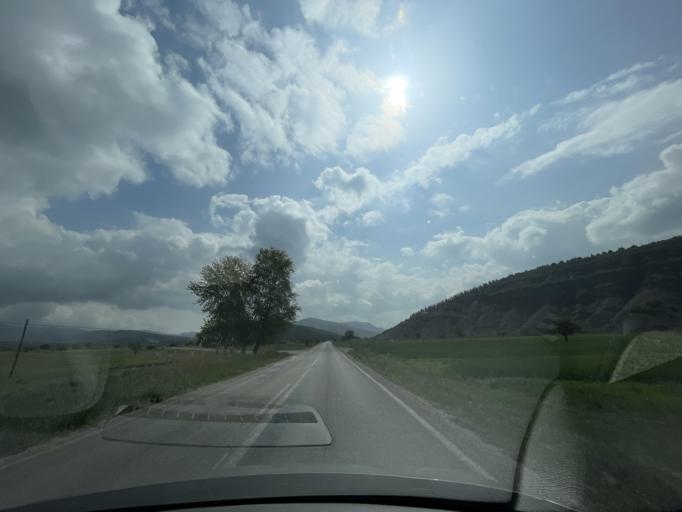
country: TR
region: Denizli
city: Acipayam
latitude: 37.5111
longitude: 29.4615
